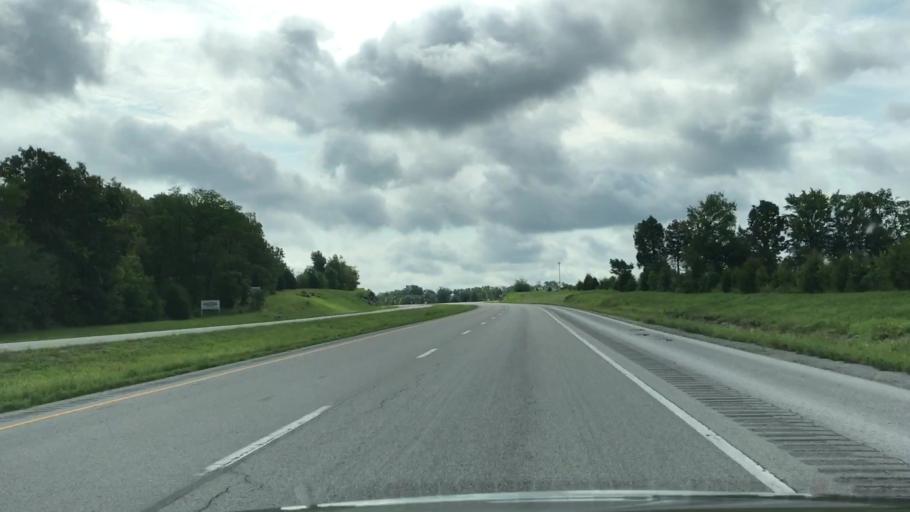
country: US
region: Kentucky
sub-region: Todd County
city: Elkton
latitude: 36.8289
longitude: -87.2247
